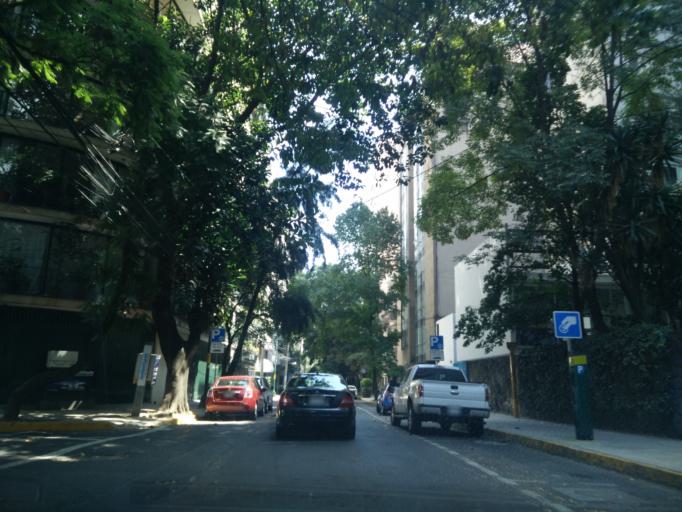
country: MX
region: Mexico City
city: Miguel Hidalgo
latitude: 19.4303
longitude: -99.2046
